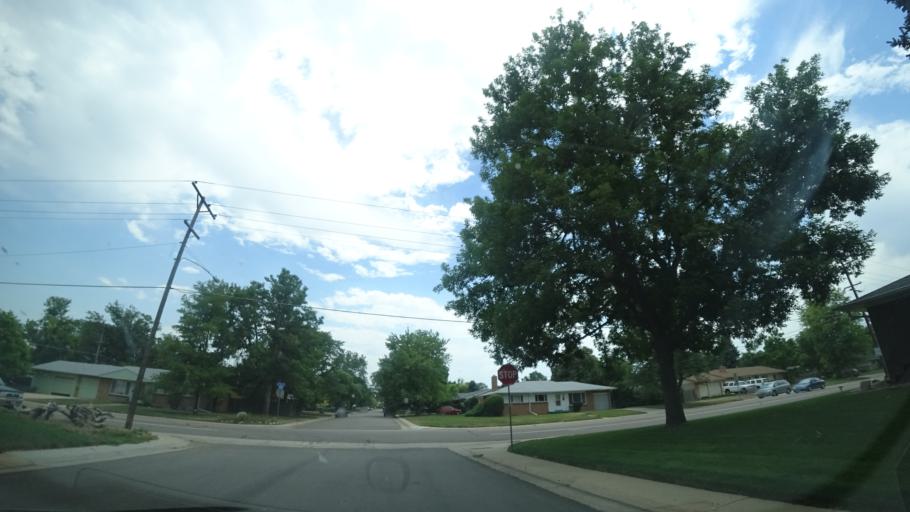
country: US
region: Colorado
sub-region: Jefferson County
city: Lakewood
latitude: 39.7188
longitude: -105.0948
